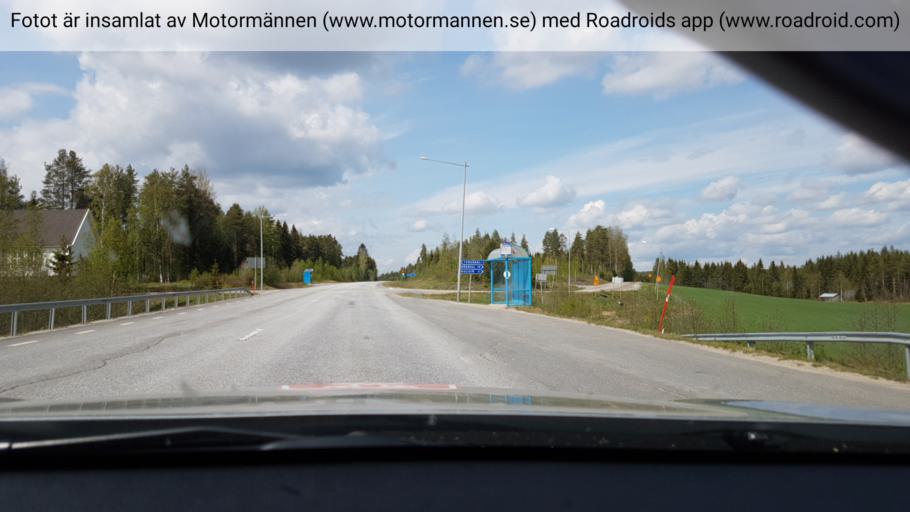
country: SE
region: Vaesterbotten
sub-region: Vannas Kommun
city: Vaennaes
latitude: 63.9973
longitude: 19.7264
